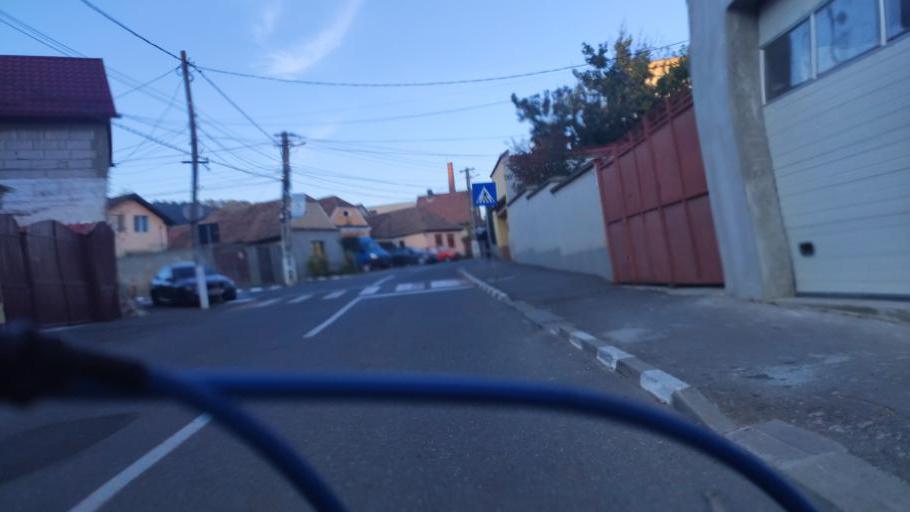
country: RO
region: Brasov
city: Codlea
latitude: 45.7033
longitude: 25.4412
